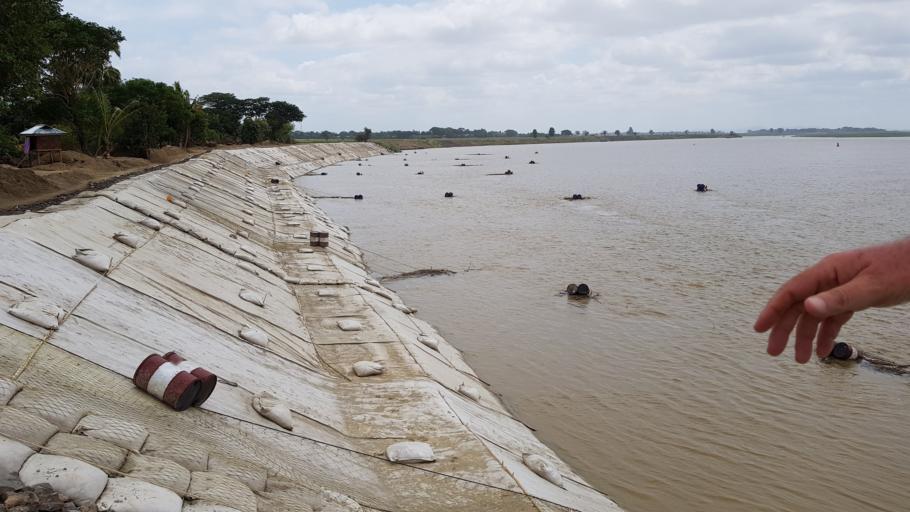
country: MM
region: Magway
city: Pakokku
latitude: 21.4314
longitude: 95.2164
